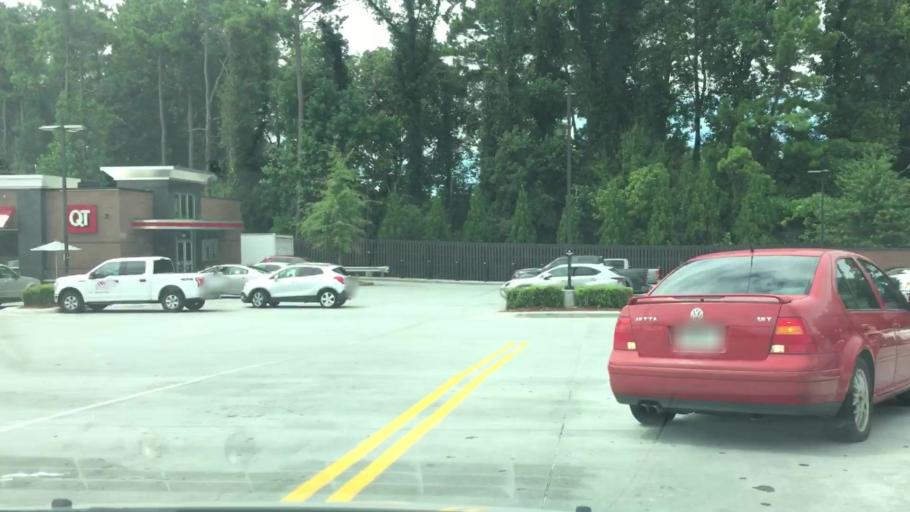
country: US
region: Georgia
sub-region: DeKalb County
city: Doraville
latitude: 33.8803
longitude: -84.2748
